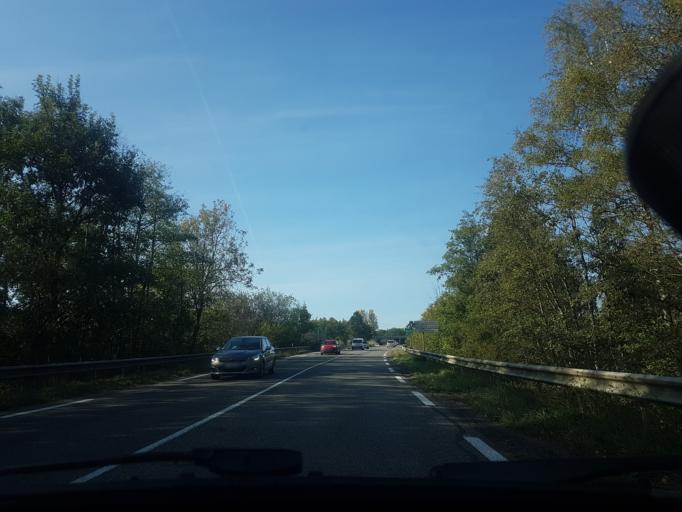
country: FR
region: Franche-Comte
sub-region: Territoire de Belfort
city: Offemont
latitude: 47.6573
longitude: 6.9079
